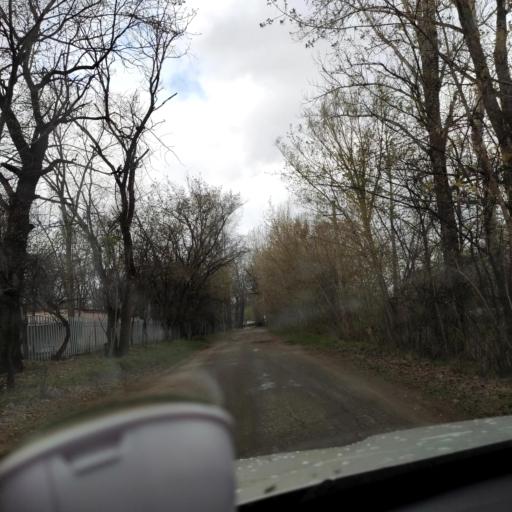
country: RU
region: Samara
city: Novokuybyshevsk
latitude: 53.1398
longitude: 49.9718
